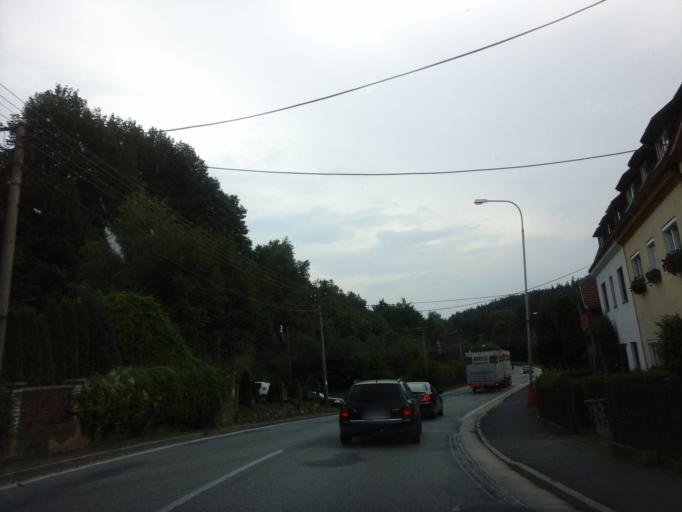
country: CZ
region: Pardubicky
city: Brnenec
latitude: 49.6180
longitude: 16.5311
